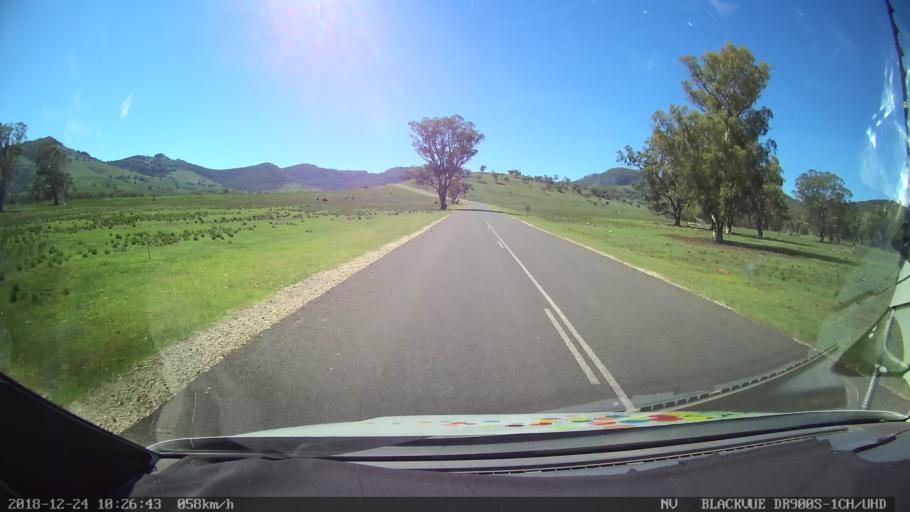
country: AU
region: New South Wales
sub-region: Liverpool Plains
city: Quirindi
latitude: -31.8119
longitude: 150.5272
